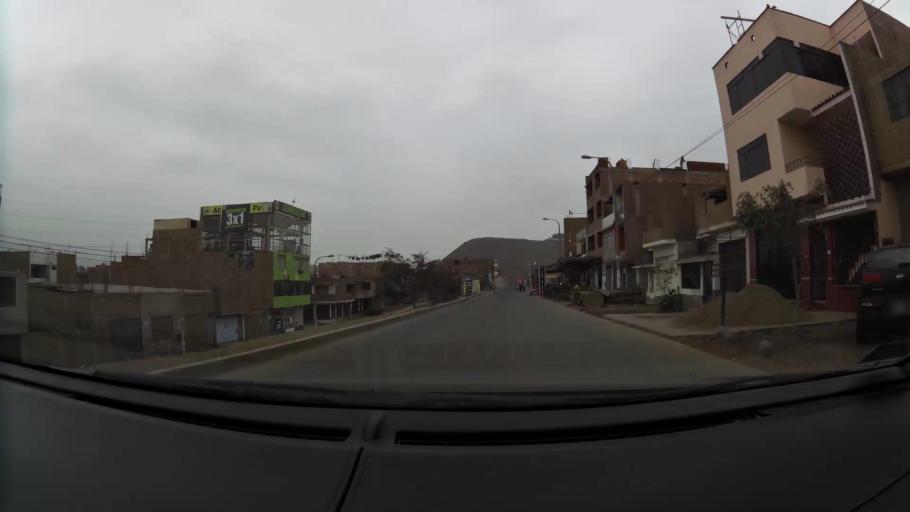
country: PE
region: Lima
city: Ventanilla
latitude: -11.9231
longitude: -77.0802
